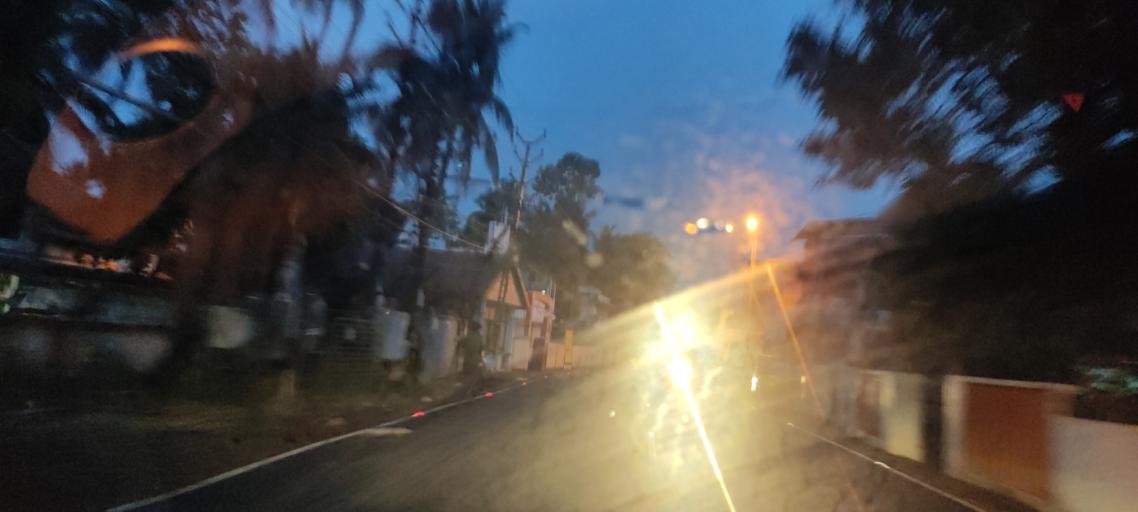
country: IN
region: Kerala
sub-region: Ernakulam
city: Cochin
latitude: 9.8973
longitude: 76.2956
